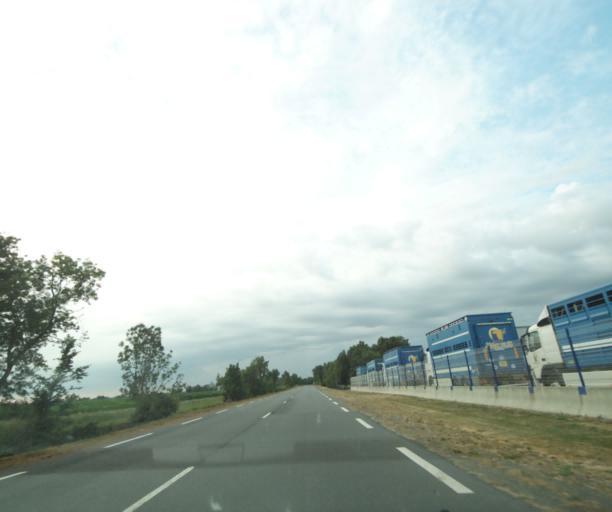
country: FR
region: Poitou-Charentes
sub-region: Departement de la Charente-Maritime
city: Marans
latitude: 46.3357
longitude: -0.9975
